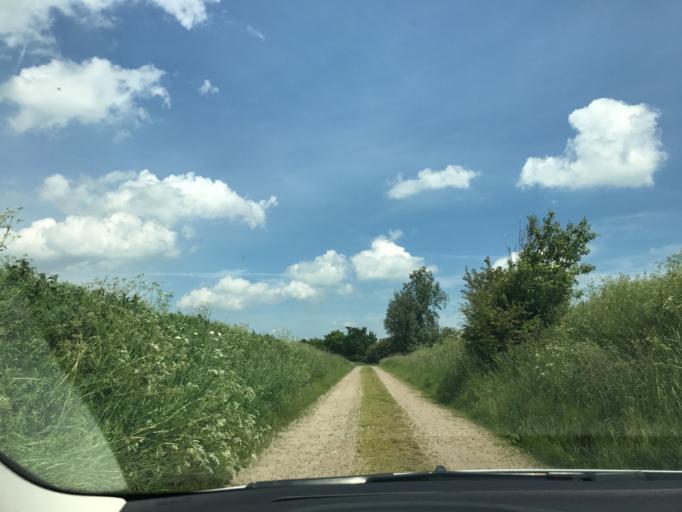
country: DE
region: Schleswig-Holstein
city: Ellhoft
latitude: 54.9301
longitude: 8.9512
